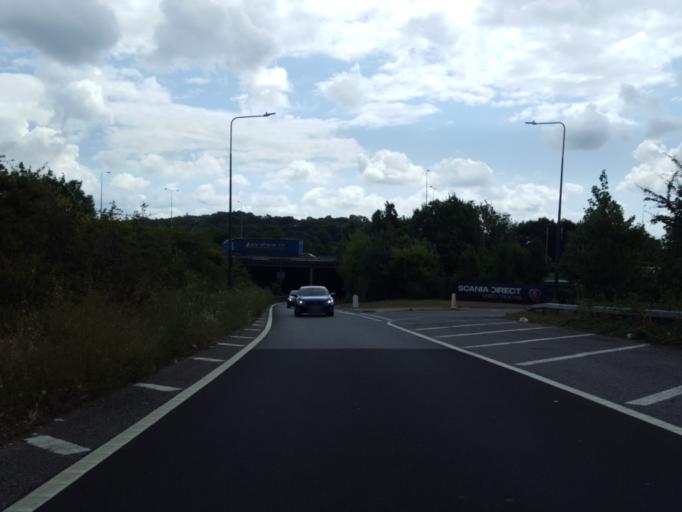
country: GB
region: England
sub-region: Kent
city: Boxley
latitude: 51.3000
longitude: 0.5141
